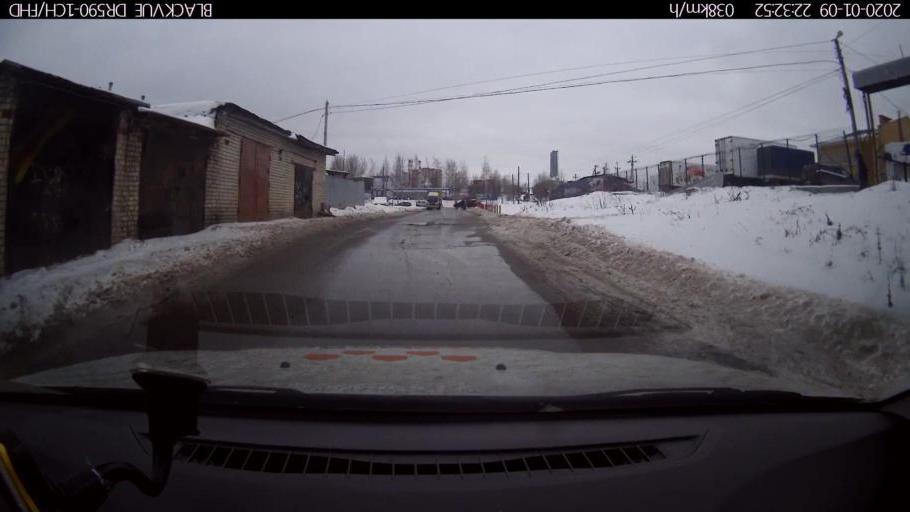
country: RU
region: Nizjnij Novgorod
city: Afonino
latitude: 56.2387
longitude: 44.0087
